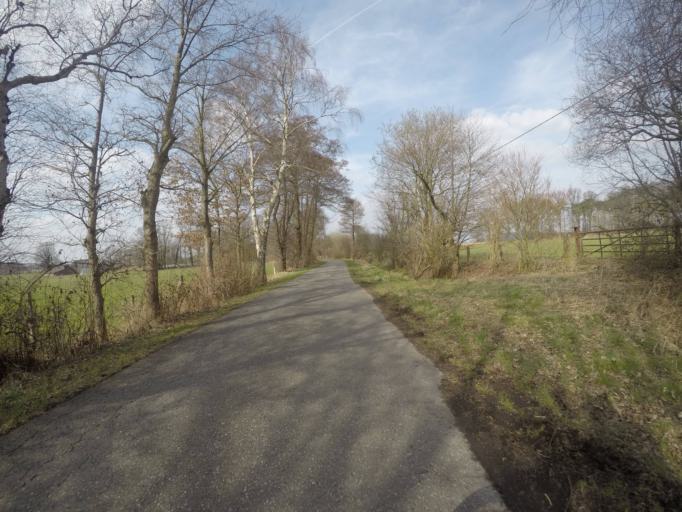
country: DE
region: North Rhine-Westphalia
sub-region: Regierungsbezirk Munster
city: Rhede
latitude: 51.8073
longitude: 6.7067
